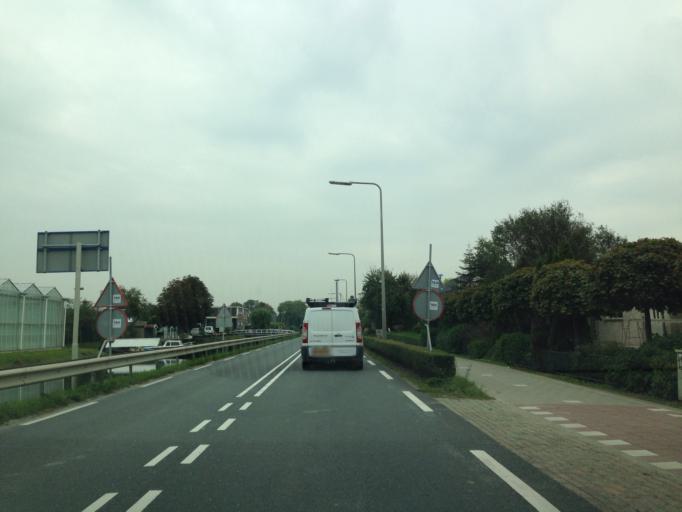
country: NL
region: South Holland
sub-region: Gemeente Westland
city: Maasdijk
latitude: 51.9708
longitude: 4.2072
